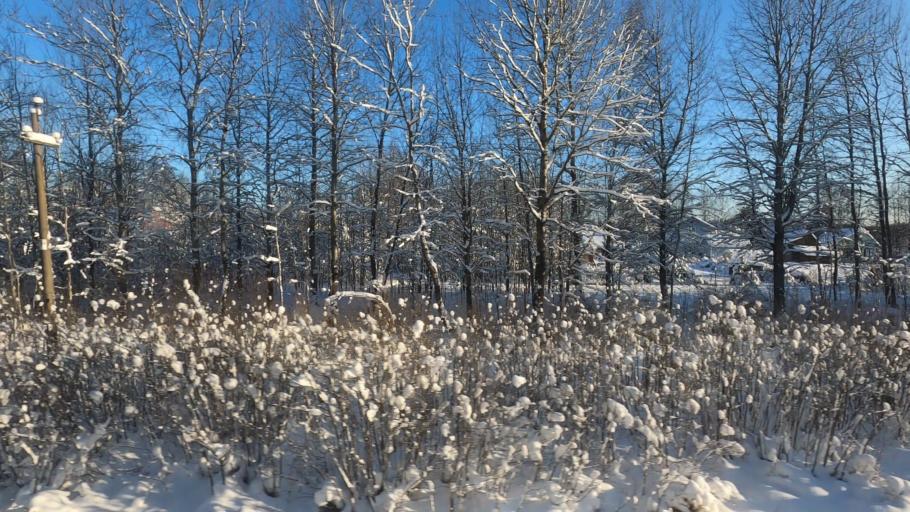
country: RU
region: Moskovskaya
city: Novo-Nikol'skoye
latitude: 56.6464
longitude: 37.5636
